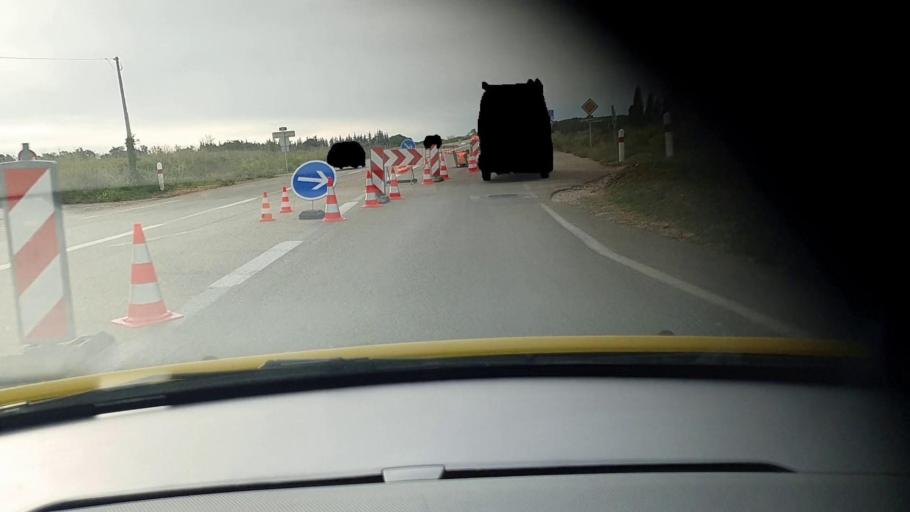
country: FR
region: Languedoc-Roussillon
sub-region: Departement du Gard
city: Caissargues
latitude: 43.7832
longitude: 4.3927
